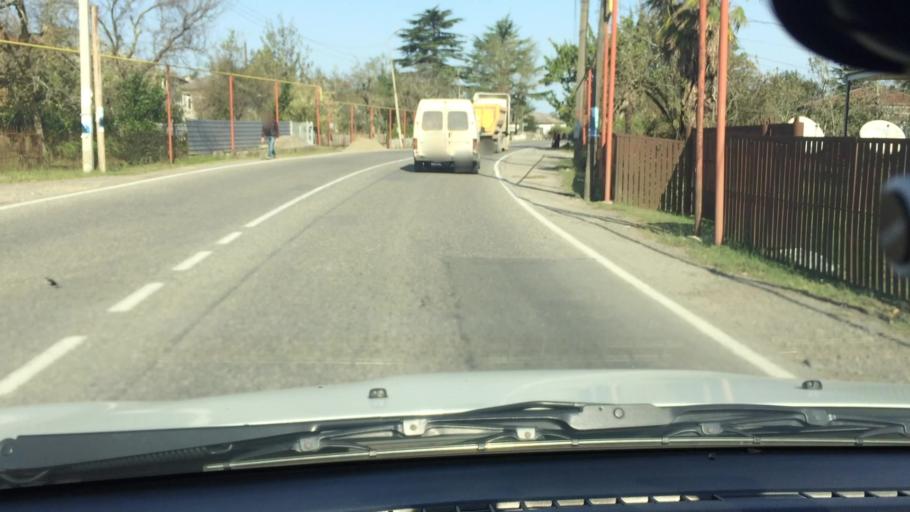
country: GE
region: Guria
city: Lanchkhuti
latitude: 42.0781
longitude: 42.0513
